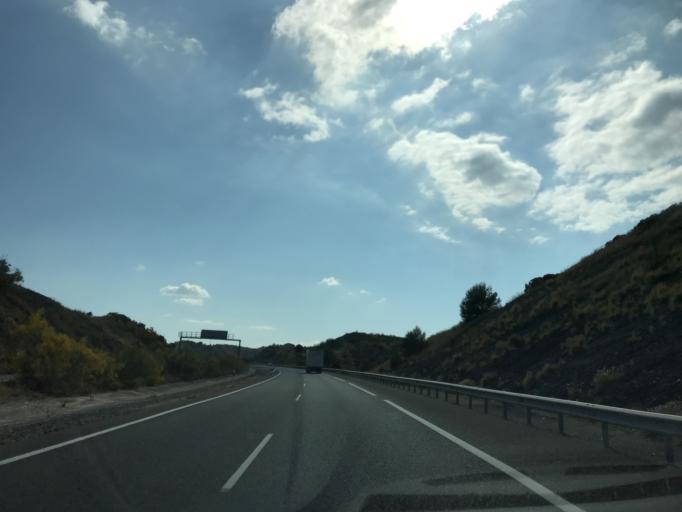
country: ES
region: Andalusia
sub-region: Provincia de Malaga
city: Istan
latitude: 36.5263
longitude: -4.9699
